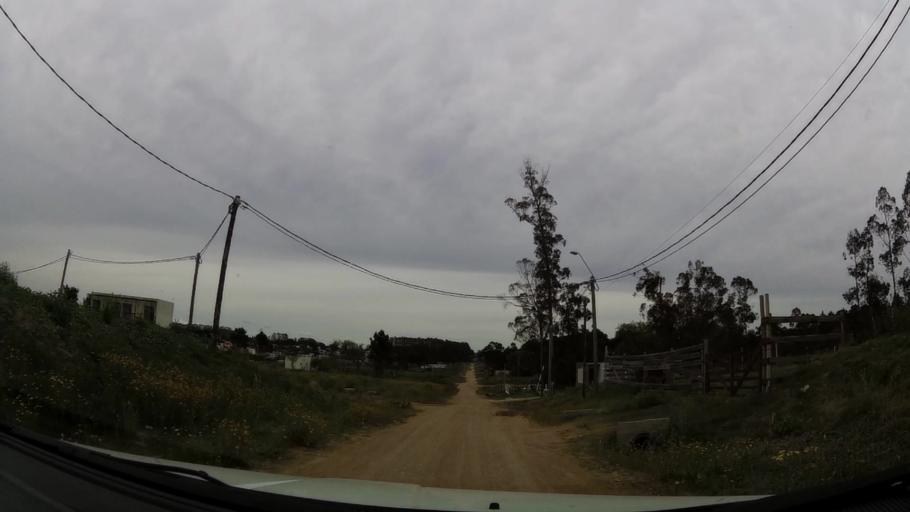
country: UY
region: Maldonado
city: Maldonado
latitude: -34.8976
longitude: -54.9889
